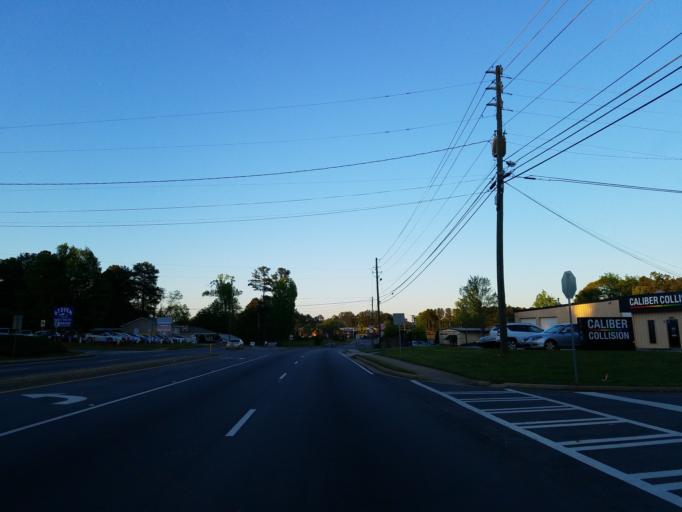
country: US
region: Georgia
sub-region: Cobb County
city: Fair Oaks
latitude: 33.9008
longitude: -84.5701
